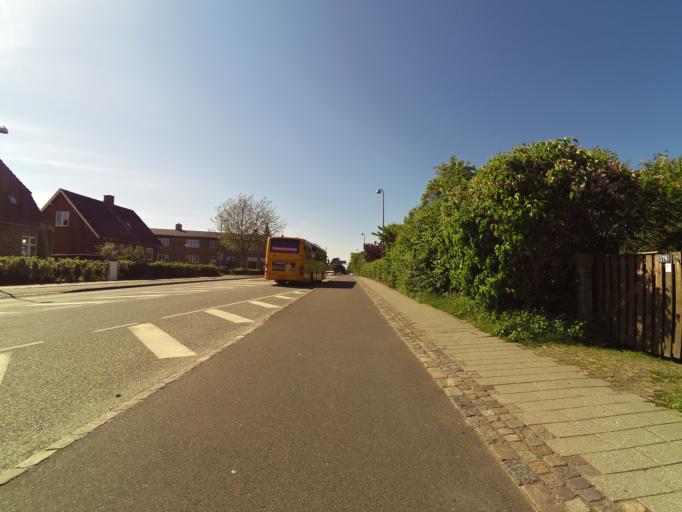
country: DK
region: Capital Region
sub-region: Gladsaxe Municipality
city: Buddinge
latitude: 55.7644
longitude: 12.4909
